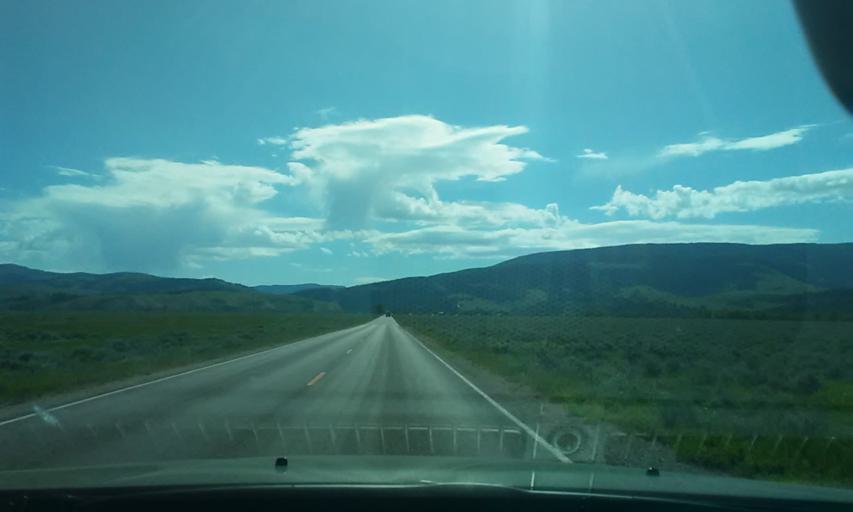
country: US
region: Wyoming
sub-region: Teton County
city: Jackson
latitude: 43.6251
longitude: -110.6519
